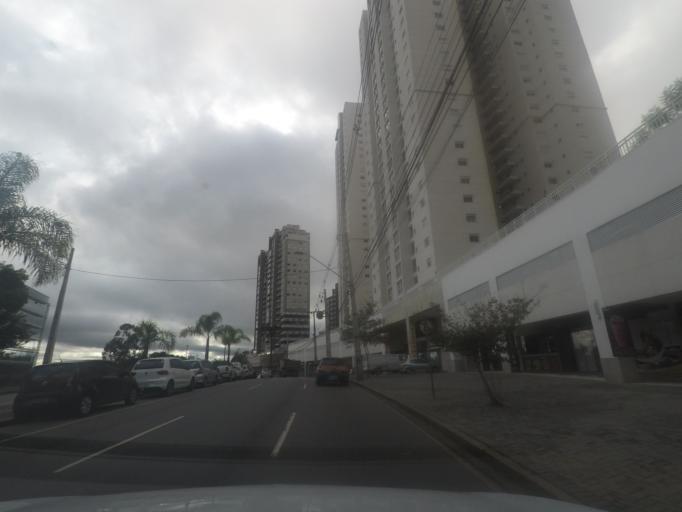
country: BR
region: Parana
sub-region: Curitiba
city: Curitiba
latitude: -25.4376
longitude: -49.2393
